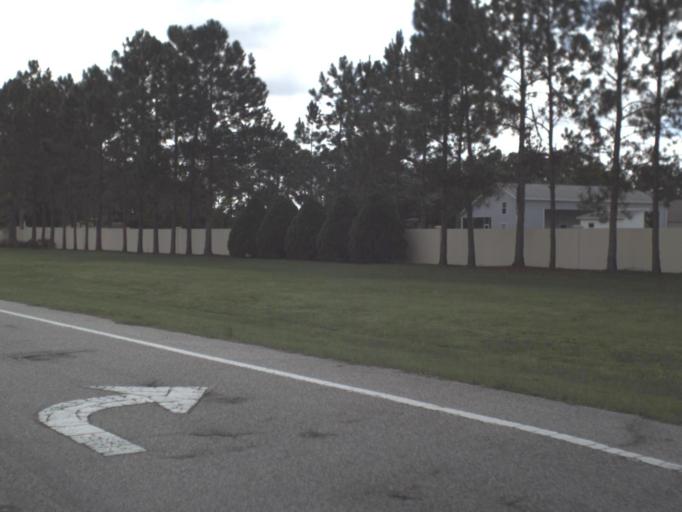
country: US
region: Florida
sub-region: Polk County
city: Polk City
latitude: 28.1793
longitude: -81.8401
